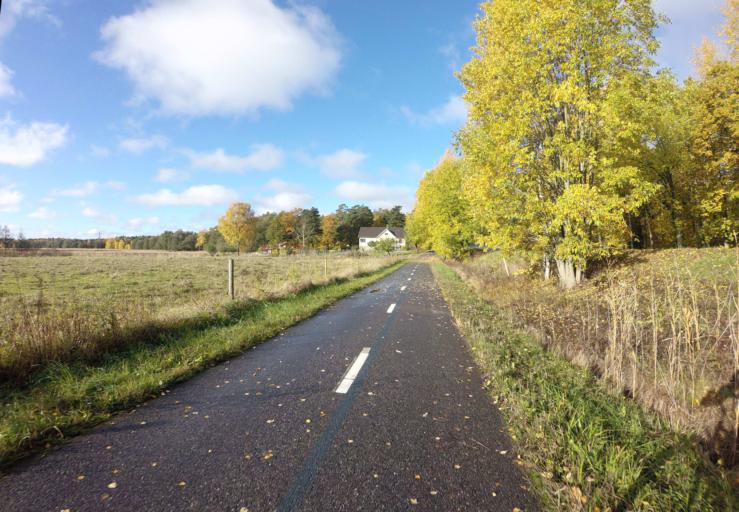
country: FI
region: Varsinais-Suomi
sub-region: Turku
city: Raisio
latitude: 60.4271
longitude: 22.1389
